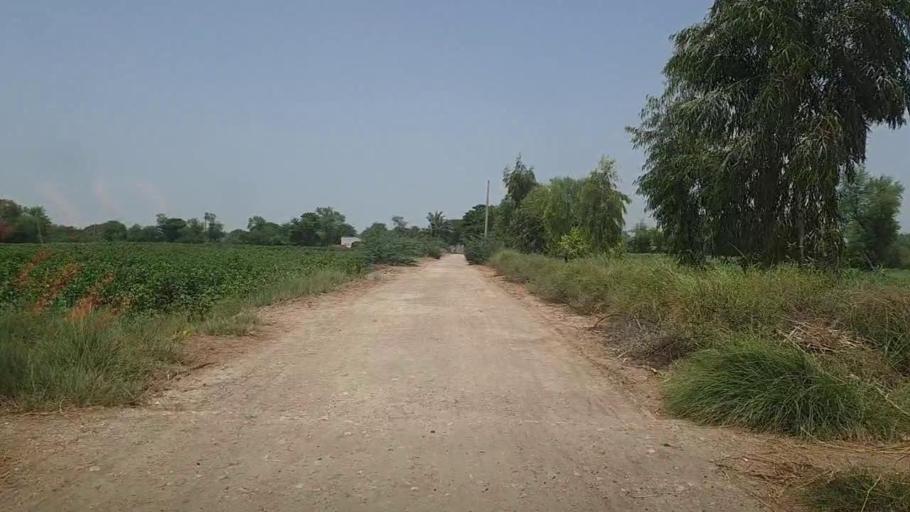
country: PK
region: Sindh
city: Pad Idan
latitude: 26.8473
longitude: 68.2964
